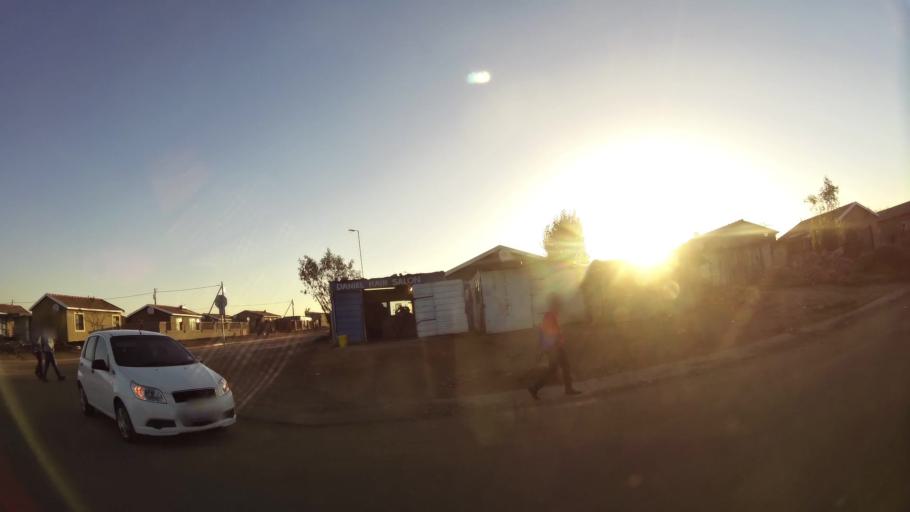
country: ZA
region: North-West
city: Ga-Rankuwa
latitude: -25.6000
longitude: 28.0920
